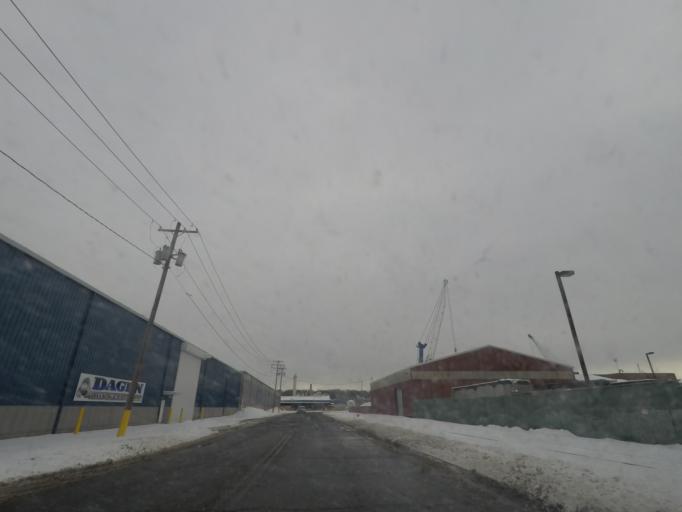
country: US
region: New York
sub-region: Rensselaer County
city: Rensselaer
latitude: 42.6280
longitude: -73.7587
